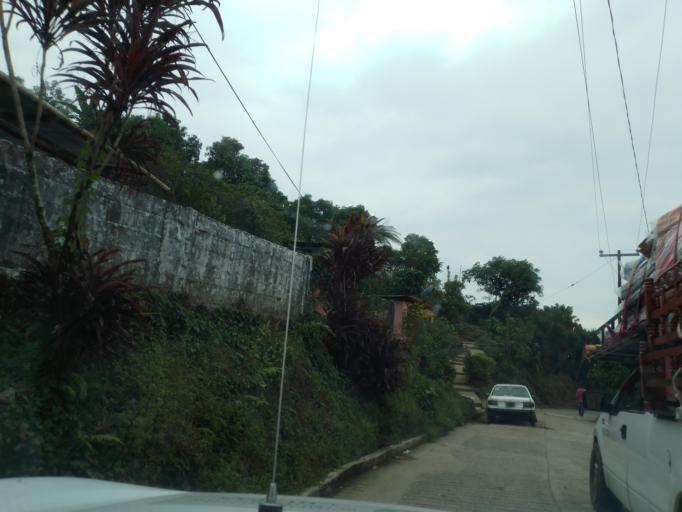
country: MX
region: Chiapas
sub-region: Union Juarez
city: Santo Domingo
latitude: 15.0550
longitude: -92.1135
